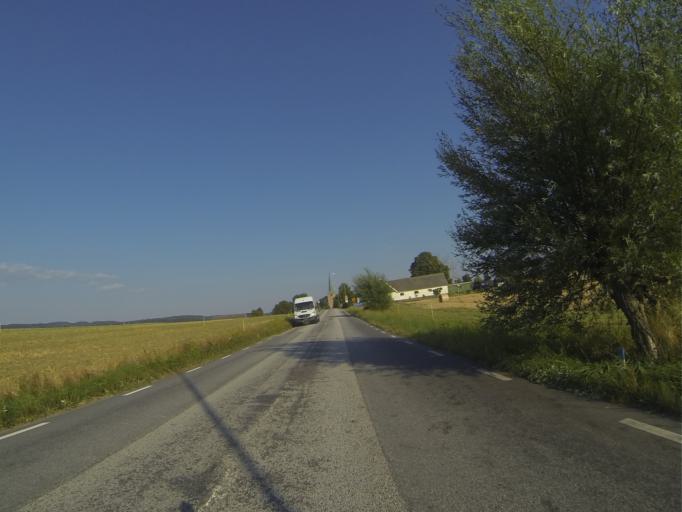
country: SE
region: Skane
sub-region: Lunds Kommun
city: Genarp
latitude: 55.6041
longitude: 13.3886
